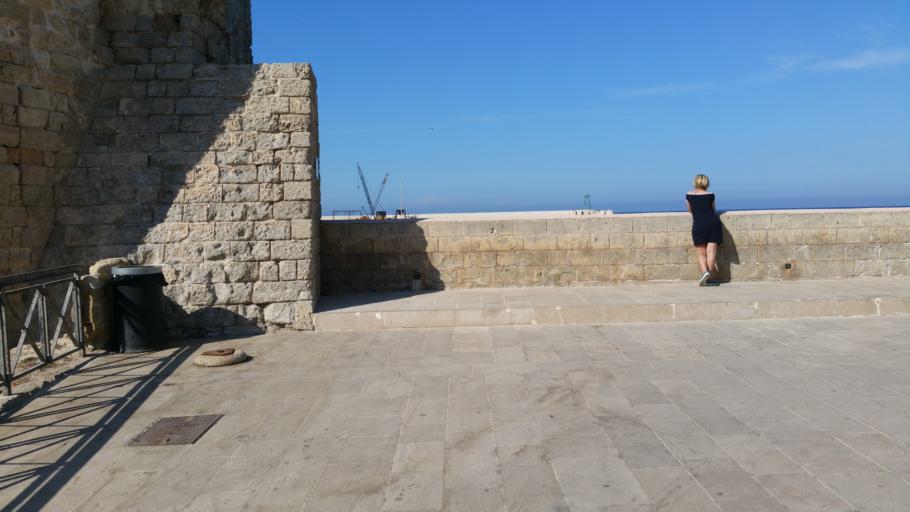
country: IT
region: Apulia
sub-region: Provincia di Bari
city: Monopoli
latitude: 40.9540
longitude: 17.3053
